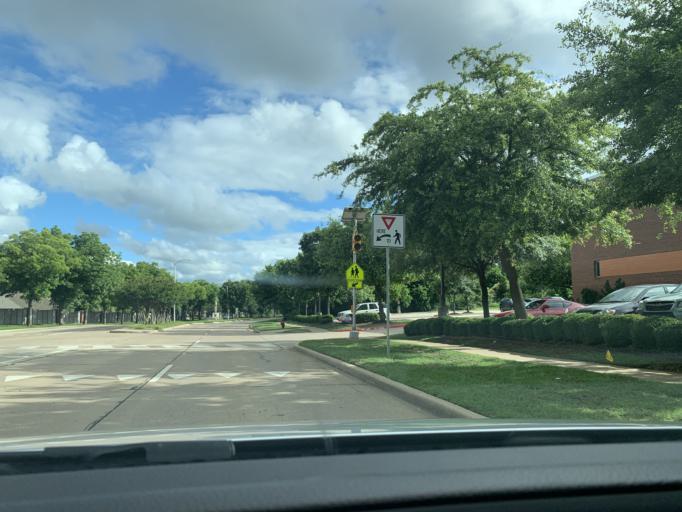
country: US
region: Texas
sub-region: Dallas County
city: Grand Prairie
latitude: 32.6613
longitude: -97.0028
